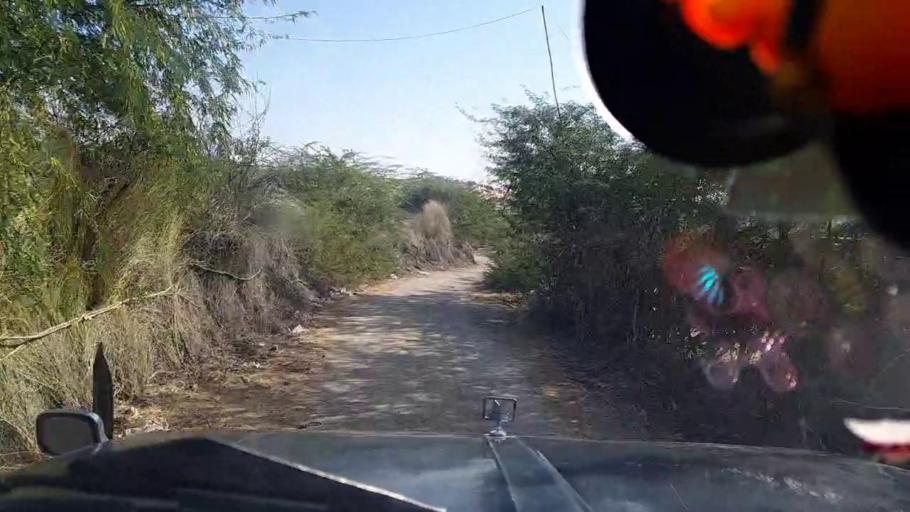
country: PK
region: Sindh
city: Diplo
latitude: 24.4698
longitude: 69.7944
